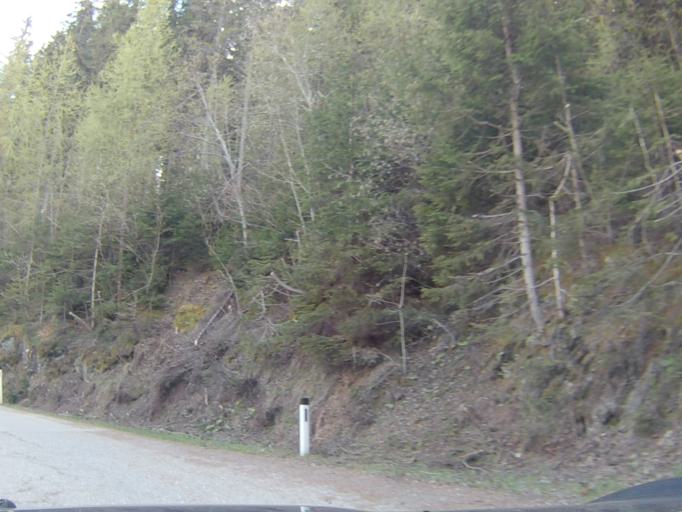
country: AT
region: Carinthia
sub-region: Politischer Bezirk Villach Land
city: Stockenboi
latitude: 46.7447
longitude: 13.5258
